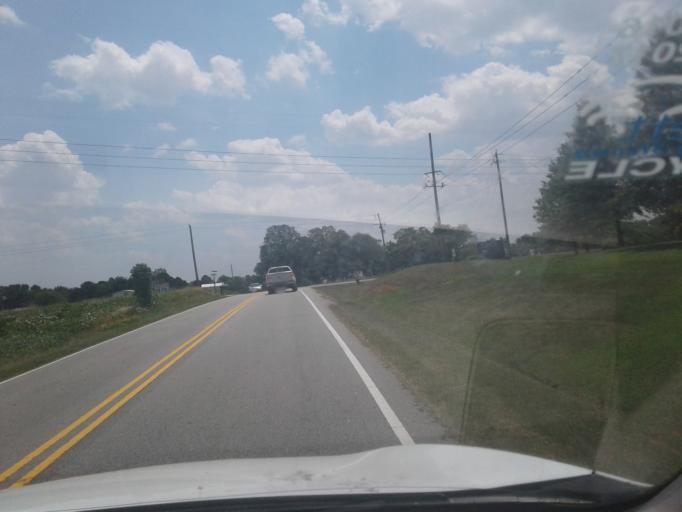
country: US
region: North Carolina
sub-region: Johnston County
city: Benson
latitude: 35.3971
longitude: -78.5430
